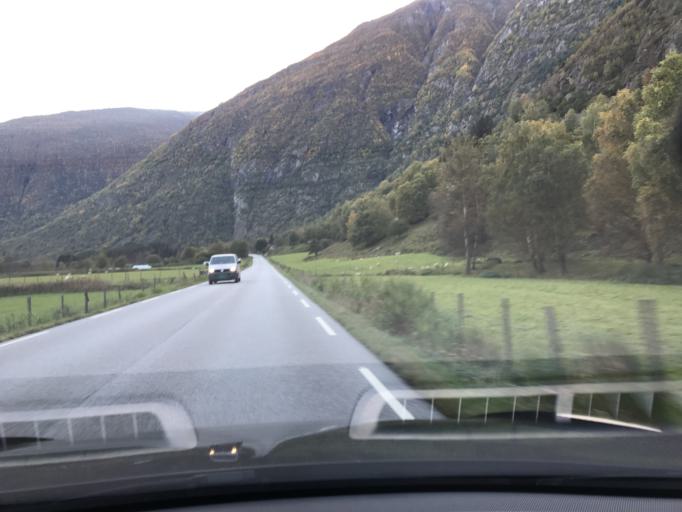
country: NO
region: Sogn og Fjordane
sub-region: Laerdal
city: Laerdalsoyri
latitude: 61.0807
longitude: 7.5060
